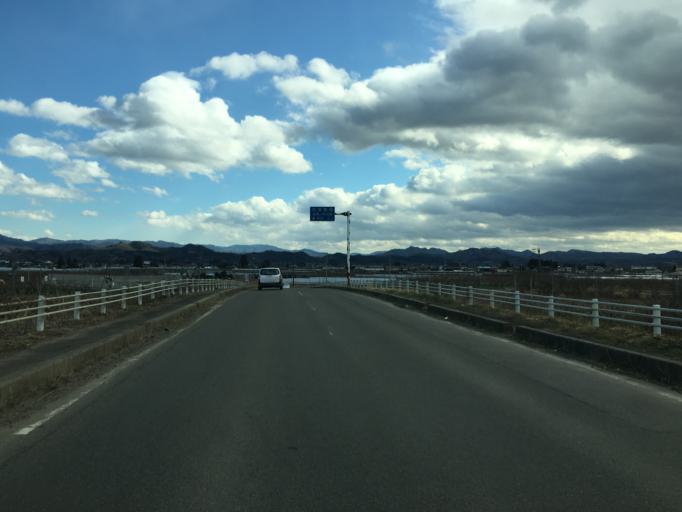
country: JP
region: Fukushima
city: Yanagawamachi-saiwaicho
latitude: 37.8611
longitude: 140.5701
